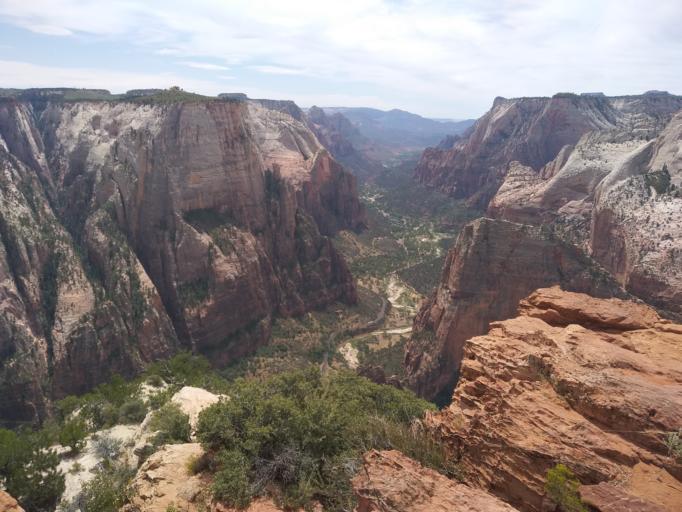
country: US
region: Utah
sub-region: Washington County
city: Hildale
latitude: 37.2783
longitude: -112.9403
